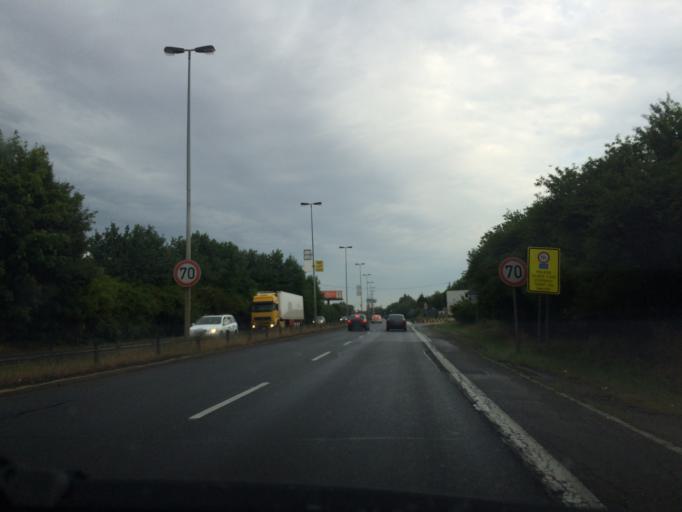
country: CZ
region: Central Bohemia
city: Tuchomerice
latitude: 50.1008
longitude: 14.2953
